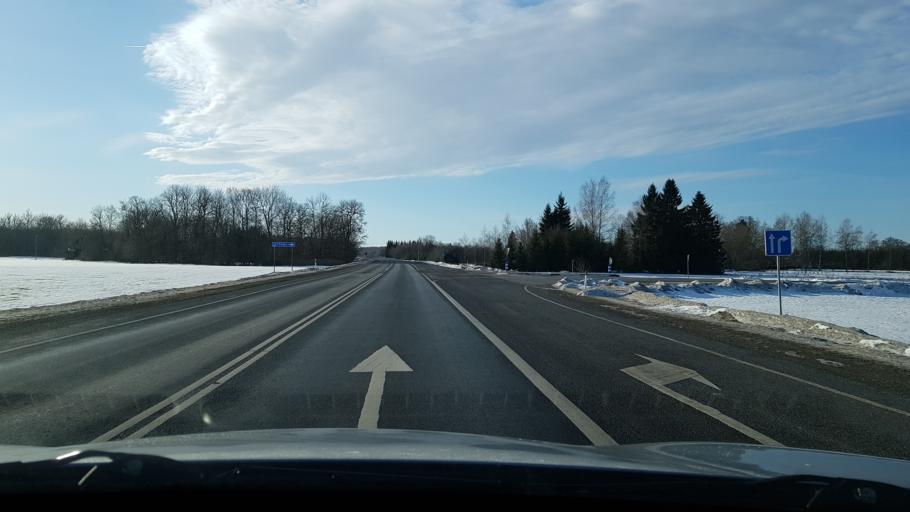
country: EE
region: Viljandimaa
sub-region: Vohma linn
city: Vohma
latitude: 58.6418
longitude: 25.5778
